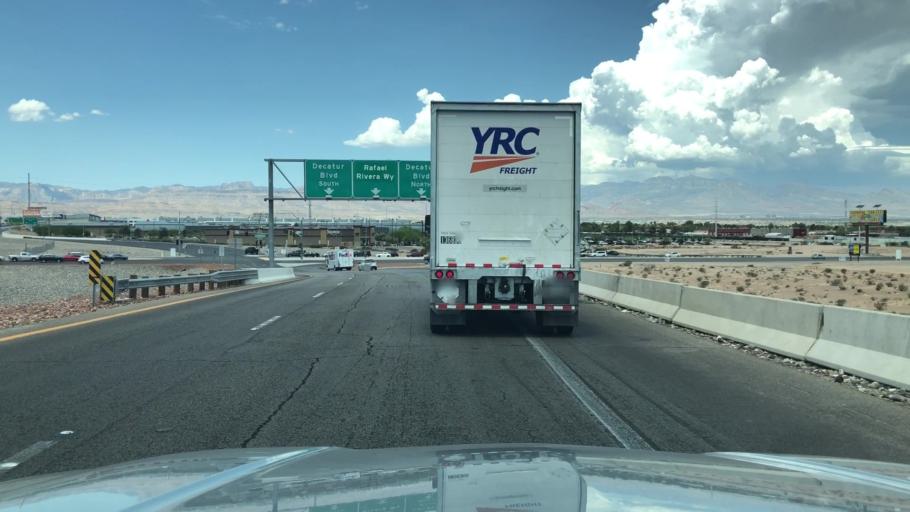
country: US
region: Nevada
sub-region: Clark County
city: Spring Valley
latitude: 36.0688
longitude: -115.2057
